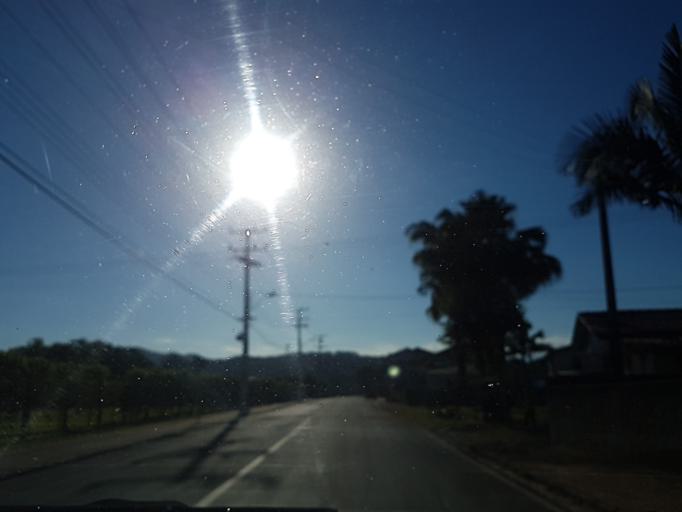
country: BR
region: Santa Catarina
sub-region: Braco Do Norte
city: Braco do Norte
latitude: -28.3300
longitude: -49.1668
